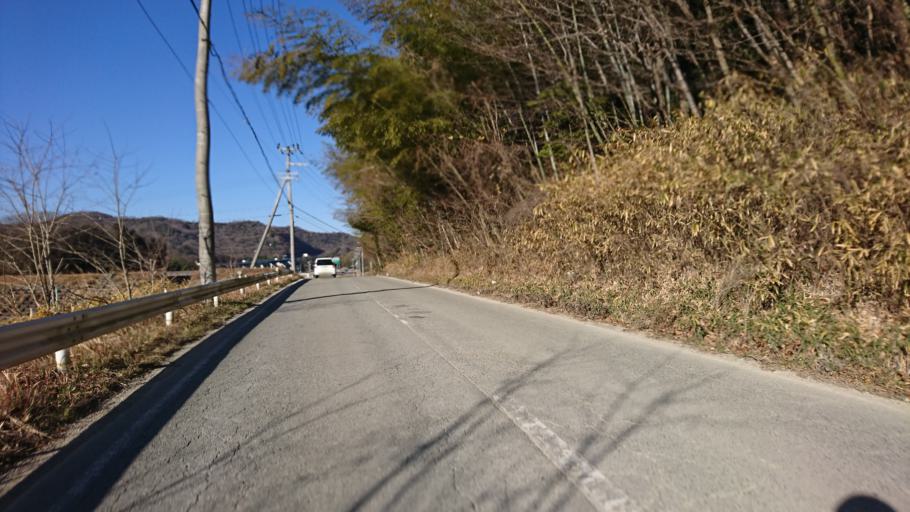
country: JP
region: Hyogo
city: Ono
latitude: 34.8393
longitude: 134.8718
